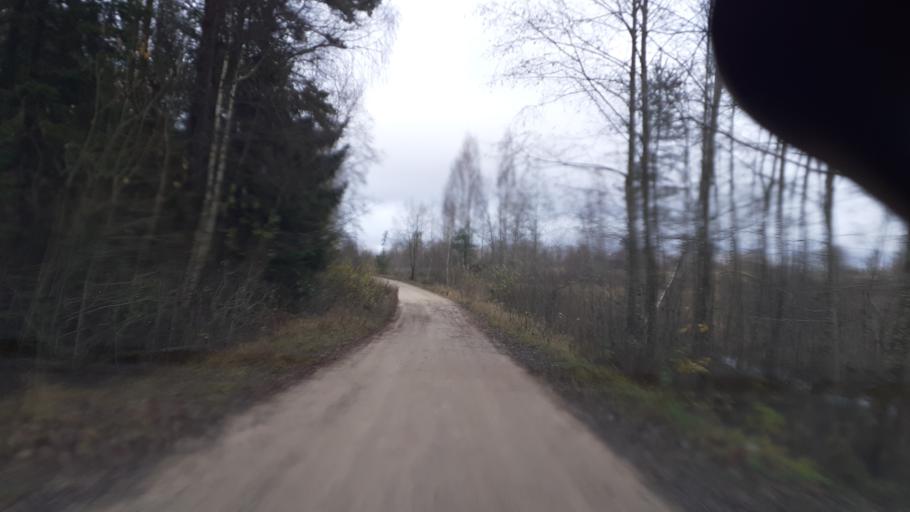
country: LV
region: Kuldigas Rajons
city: Kuldiga
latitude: 57.0372
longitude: 21.8801
